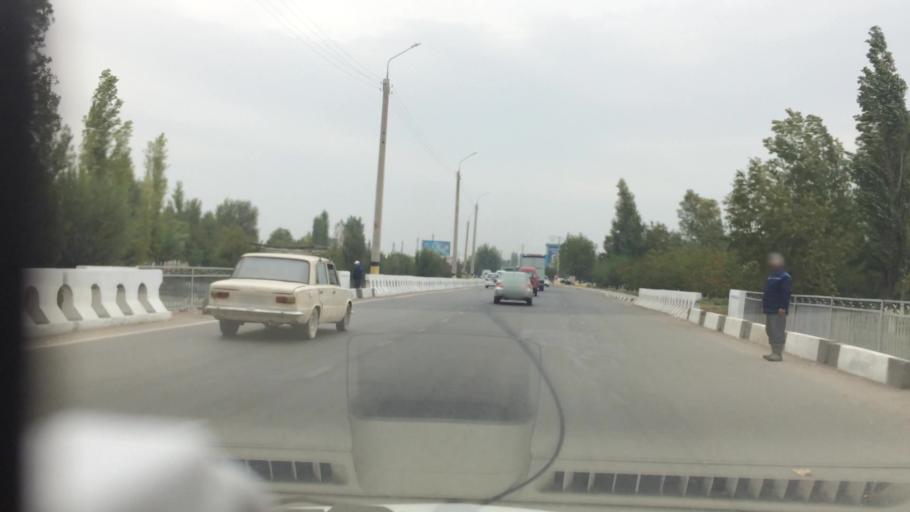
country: UZ
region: Toshkent
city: Salor
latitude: 41.3064
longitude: 69.3419
